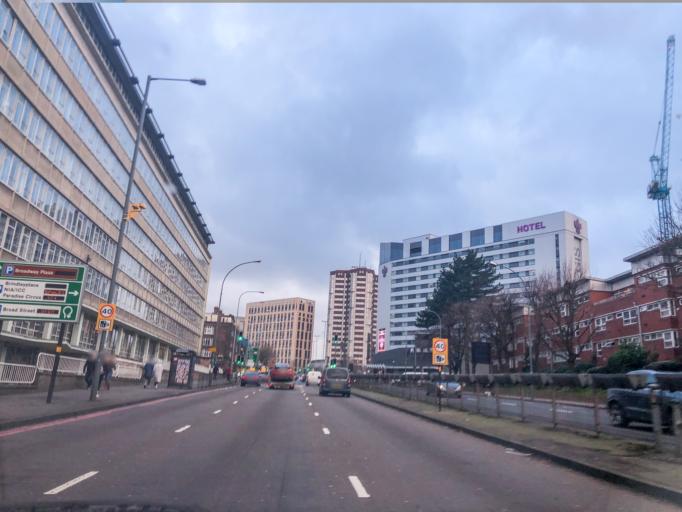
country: GB
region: England
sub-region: City and Borough of Birmingham
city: Birmingham
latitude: 52.4720
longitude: -1.9149
